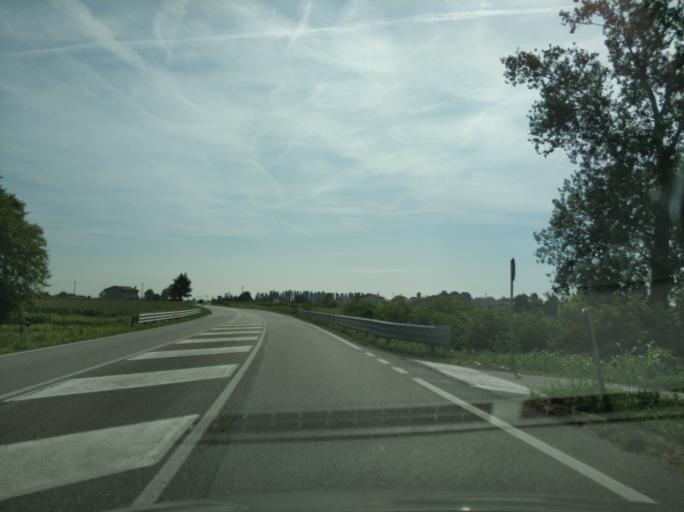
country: IT
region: Veneto
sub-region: Provincia di Padova
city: Correzzola
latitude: 45.2153
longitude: 12.0746
